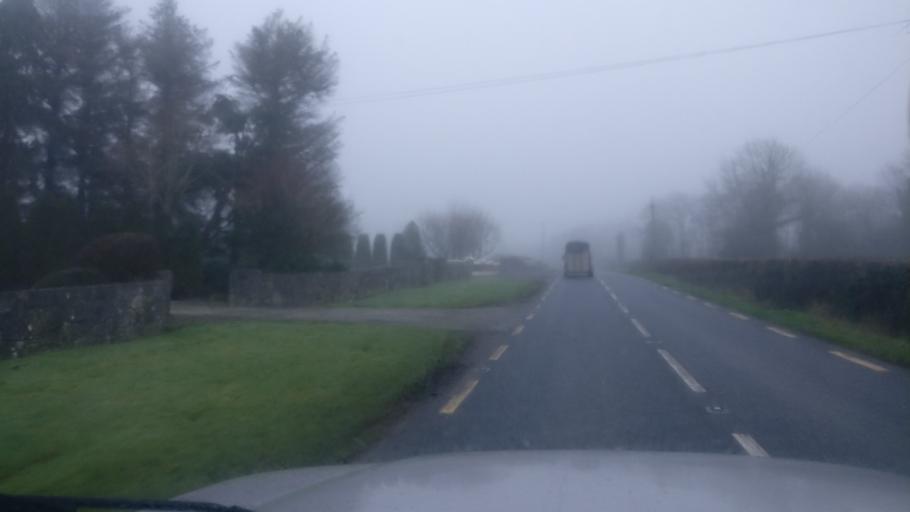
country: IE
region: Connaught
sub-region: County Galway
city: Loughrea
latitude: 53.1450
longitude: -8.6965
